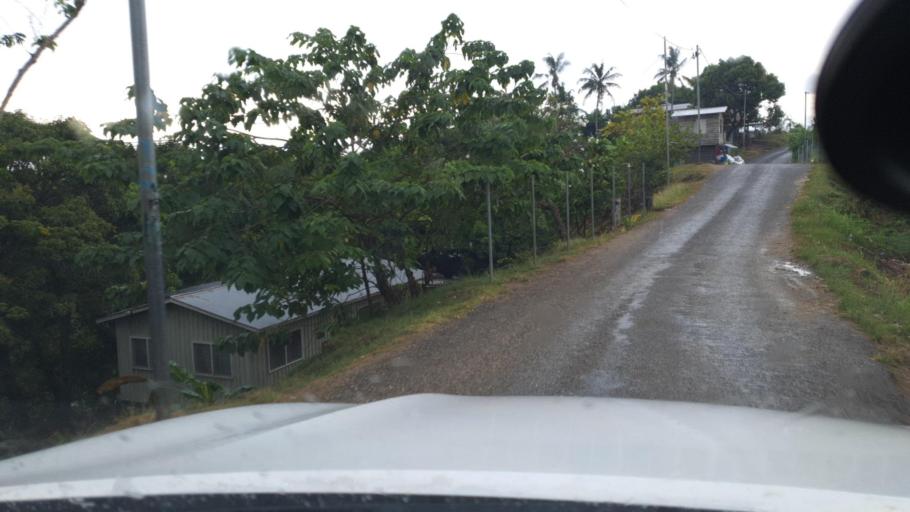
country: SB
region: Guadalcanal
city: Honiara
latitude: -9.4425
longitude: 159.9481
